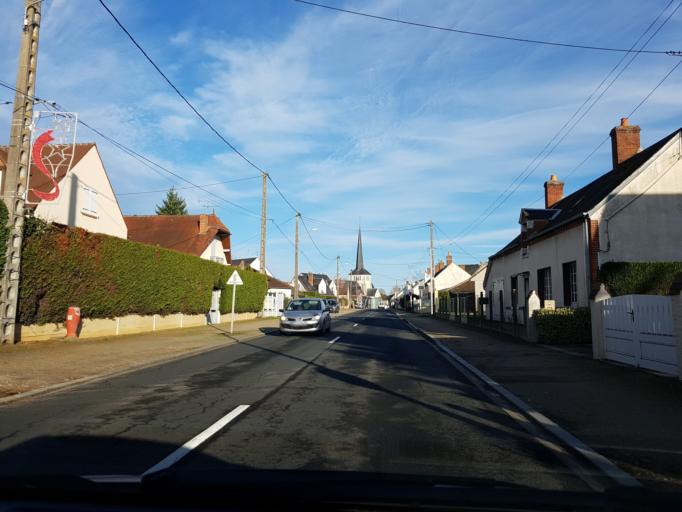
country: FR
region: Centre
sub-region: Departement du Loiret
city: Saint-Pere-sur-Loire
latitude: 47.7646
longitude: 2.3641
